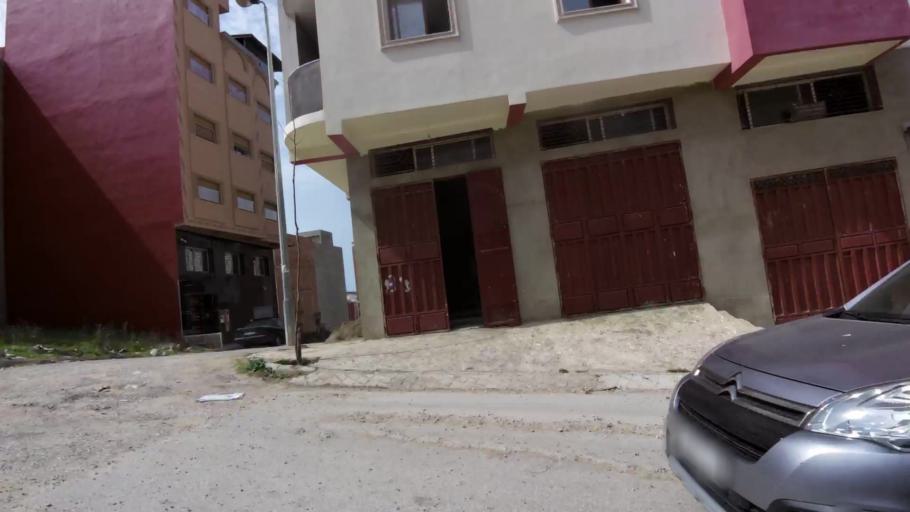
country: MA
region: Tanger-Tetouan
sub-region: Tanger-Assilah
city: Tangier
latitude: 35.7407
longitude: -5.8379
